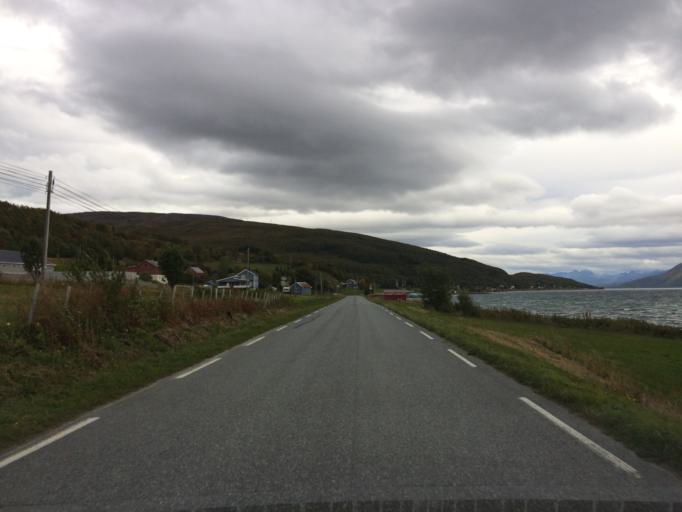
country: NO
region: Troms
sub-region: Sorreisa
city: Sorreisa
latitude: 69.5272
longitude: 18.2793
